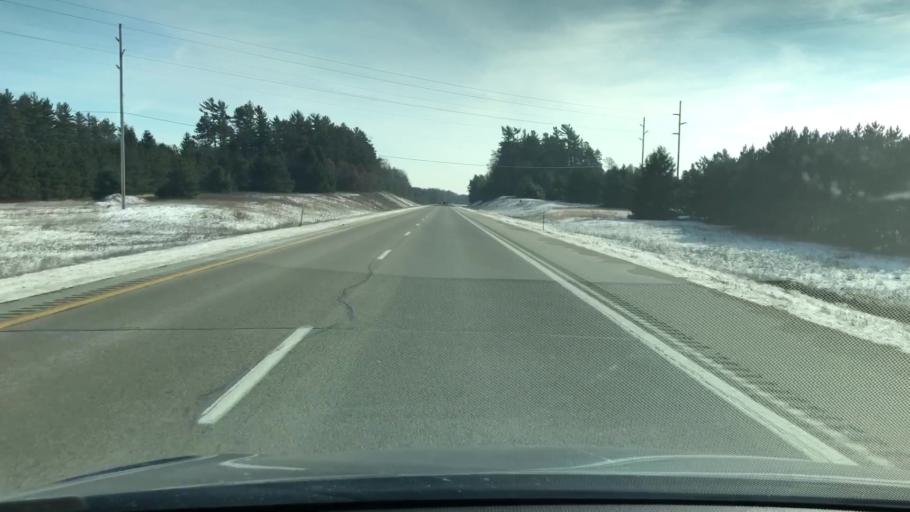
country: US
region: Michigan
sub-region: Roscommon County
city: Roscommon
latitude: 44.5391
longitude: -84.6910
